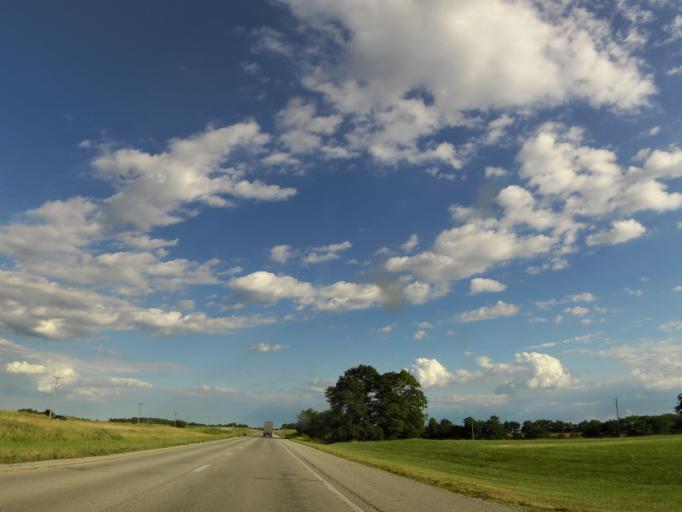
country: US
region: Missouri
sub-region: Lincoln County
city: Troy
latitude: 39.1768
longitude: -90.9850
